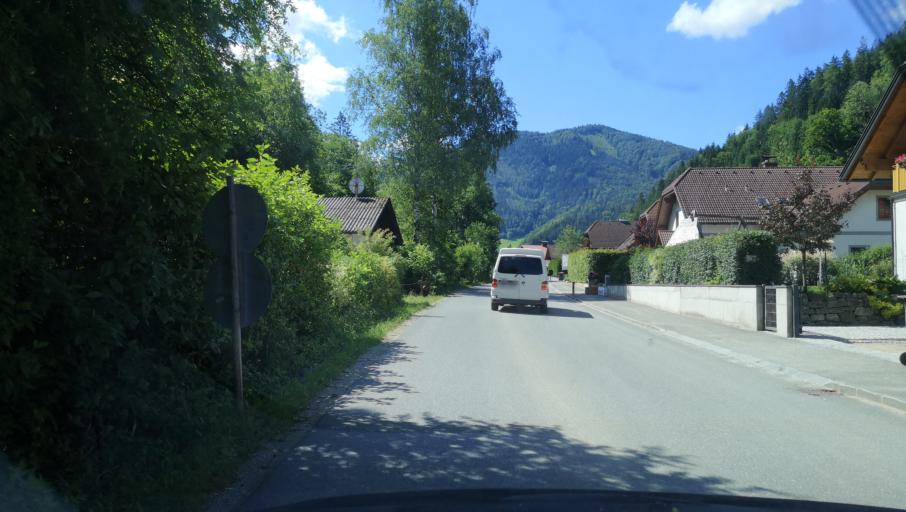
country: AT
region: Lower Austria
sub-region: Politischer Bezirk Scheibbs
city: Gresten
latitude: 47.9402
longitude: 15.0279
